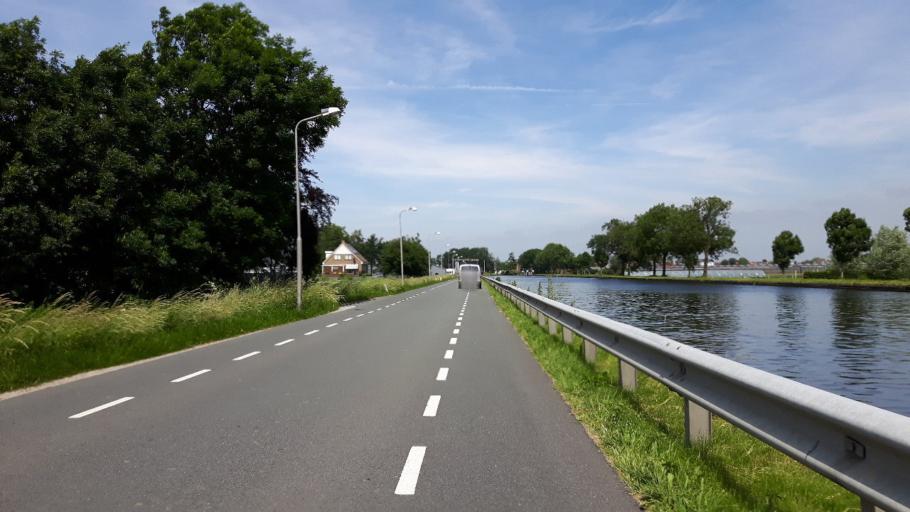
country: NL
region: South Holland
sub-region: Gemeente Nieuwkoop
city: Nieuwkoop
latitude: 52.1908
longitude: 4.7357
